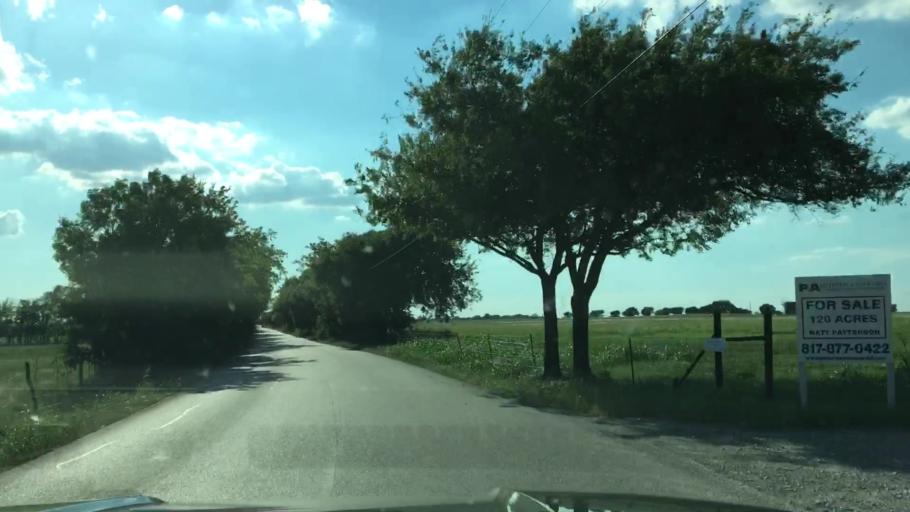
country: US
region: Texas
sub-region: Tarrant County
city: Haslet
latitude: 33.0161
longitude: -97.3626
